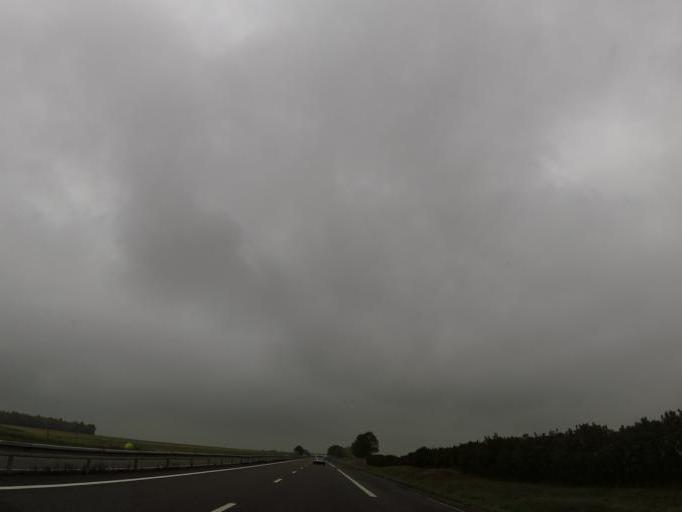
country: FR
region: Champagne-Ardenne
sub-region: Departement de la Marne
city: Suippes
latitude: 49.0517
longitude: 4.6764
